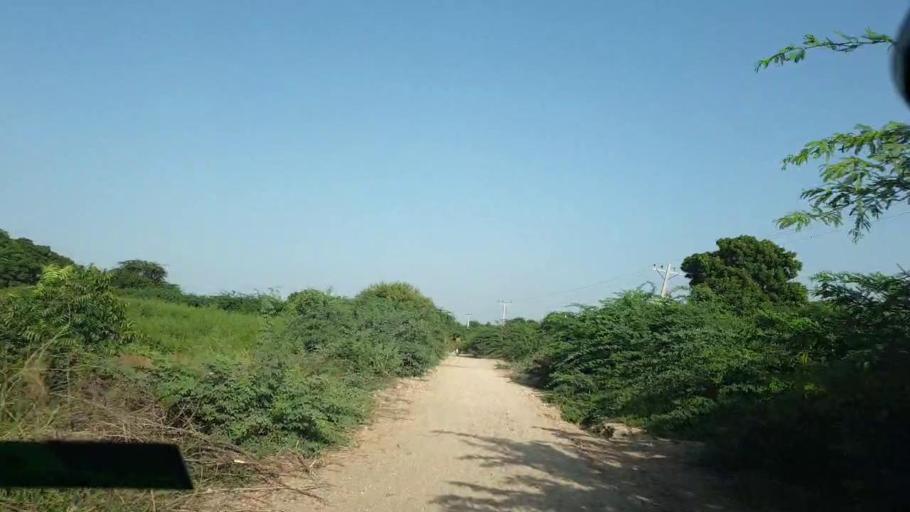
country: PK
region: Sindh
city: Naukot
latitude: 24.7319
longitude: 69.2538
